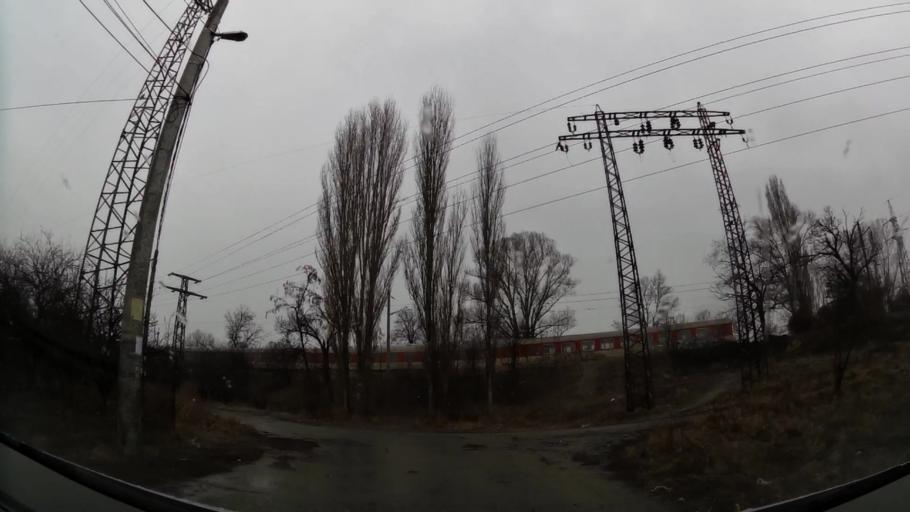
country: BG
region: Sofia-Capital
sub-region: Stolichna Obshtina
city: Sofia
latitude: 42.6628
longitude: 23.4228
